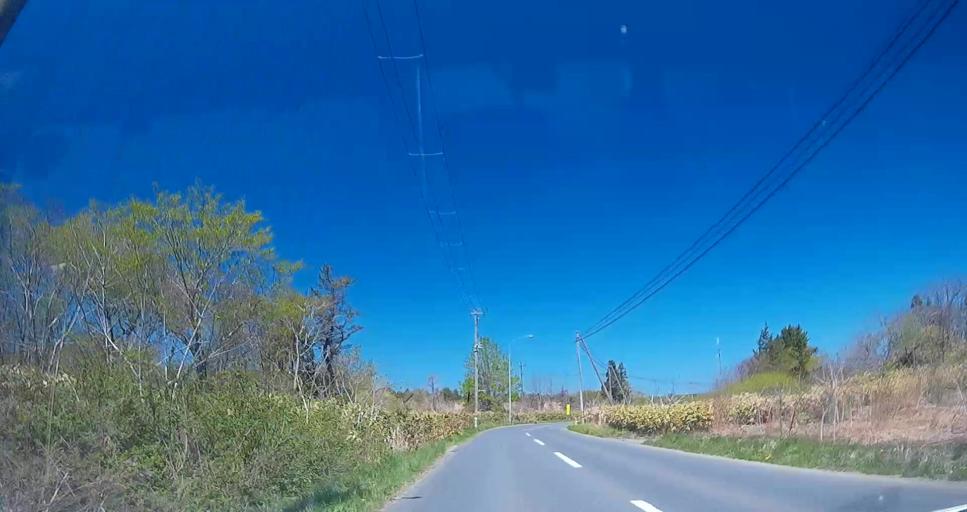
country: JP
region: Aomori
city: Misawa
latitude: 40.9286
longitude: 141.3755
